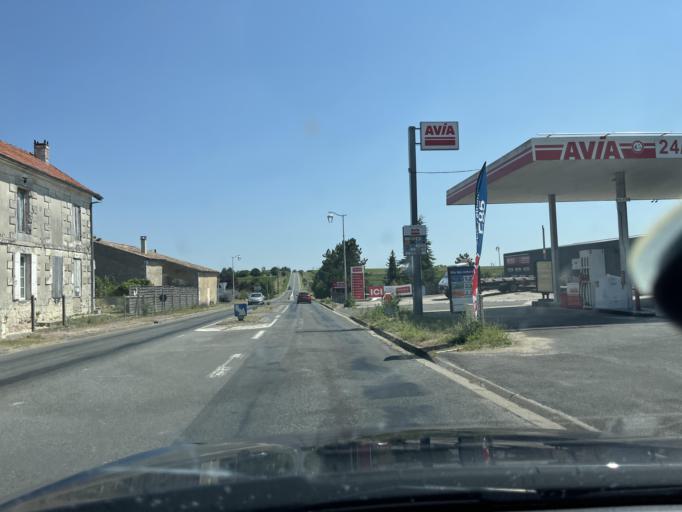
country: FR
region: Poitou-Charentes
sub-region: Departement de la Charente-Maritime
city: Mortagne-sur-Gironde
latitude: 45.4542
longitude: -0.6873
